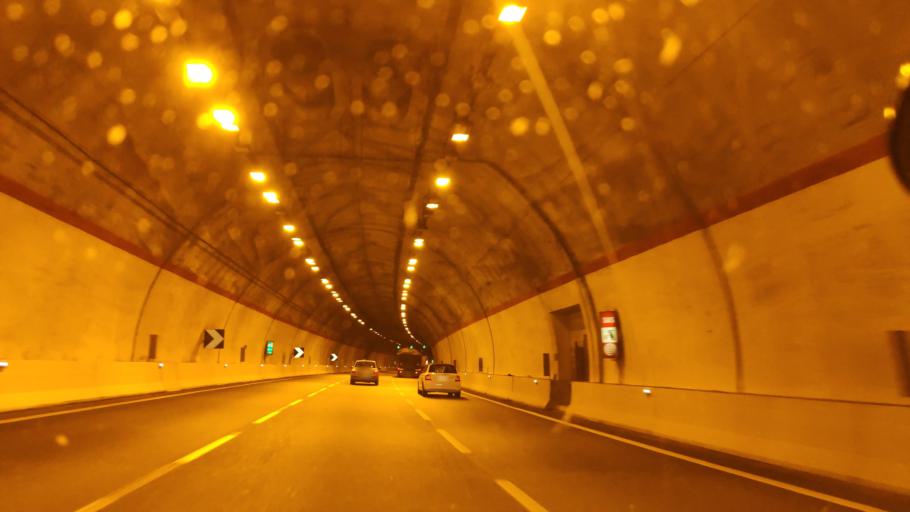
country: IT
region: Campania
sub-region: Provincia di Salerno
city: Contursi Terme
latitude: 40.6255
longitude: 15.2386
